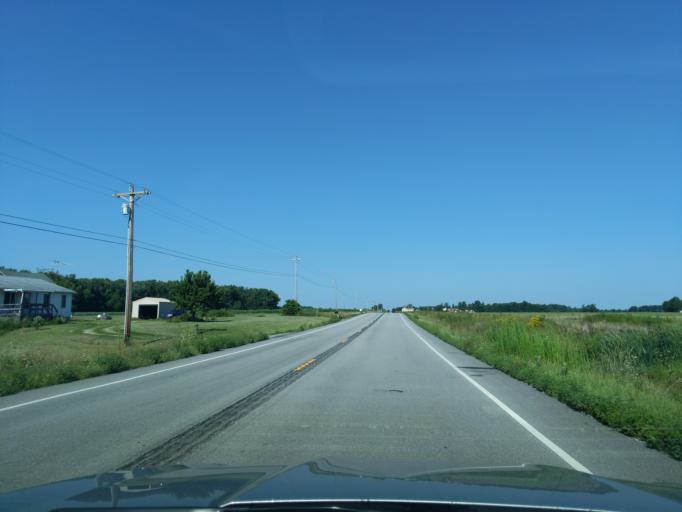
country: US
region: Indiana
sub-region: Ripley County
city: Versailles
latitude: 39.0749
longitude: -85.2843
